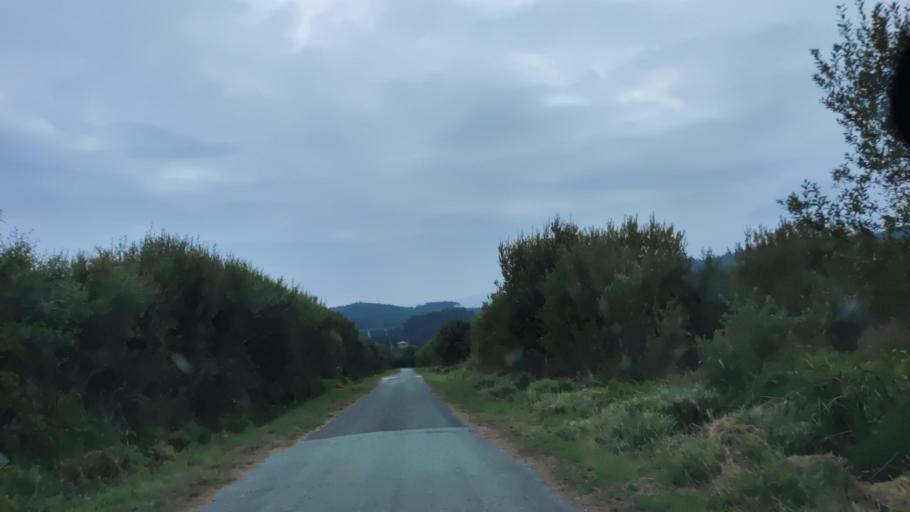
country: ES
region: Galicia
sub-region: Provincia da Coruna
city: Rois
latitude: 42.7150
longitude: -8.7115
